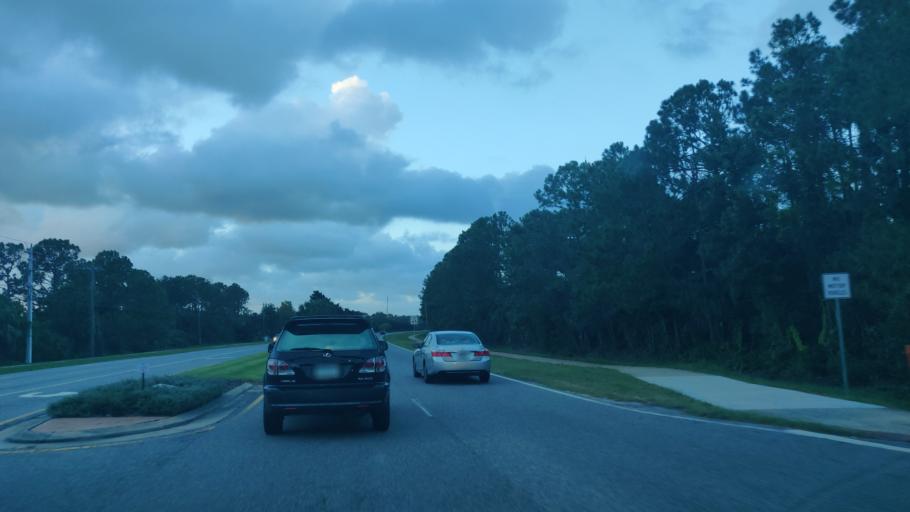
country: US
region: Florida
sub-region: Flagler County
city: Bunnell
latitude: 29.5182
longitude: -81.2242
